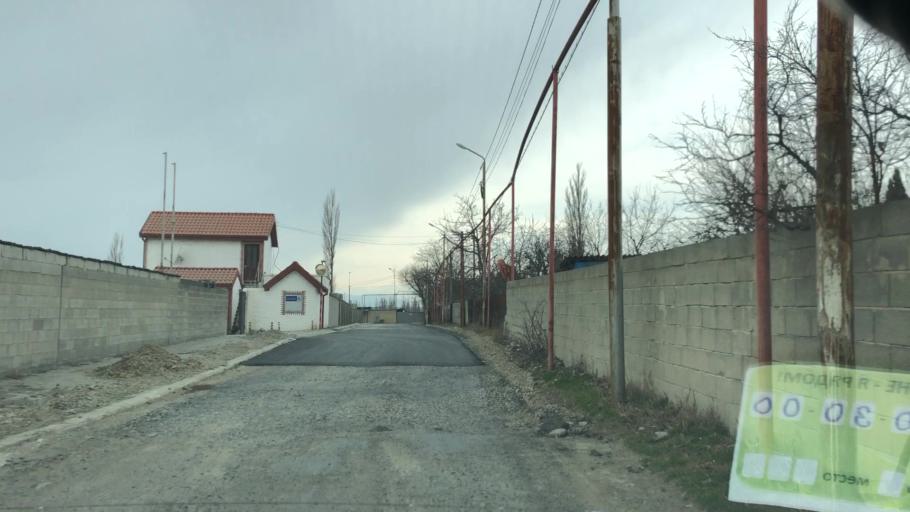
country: GE
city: Didi Lilo
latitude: 41.7012
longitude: 44.9261
